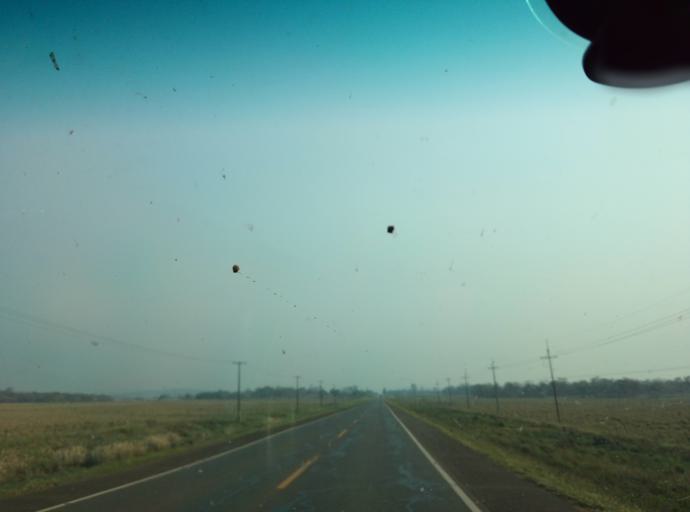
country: PY
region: Caaguazu
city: Carayao
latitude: -25.1314
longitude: -56.3545
